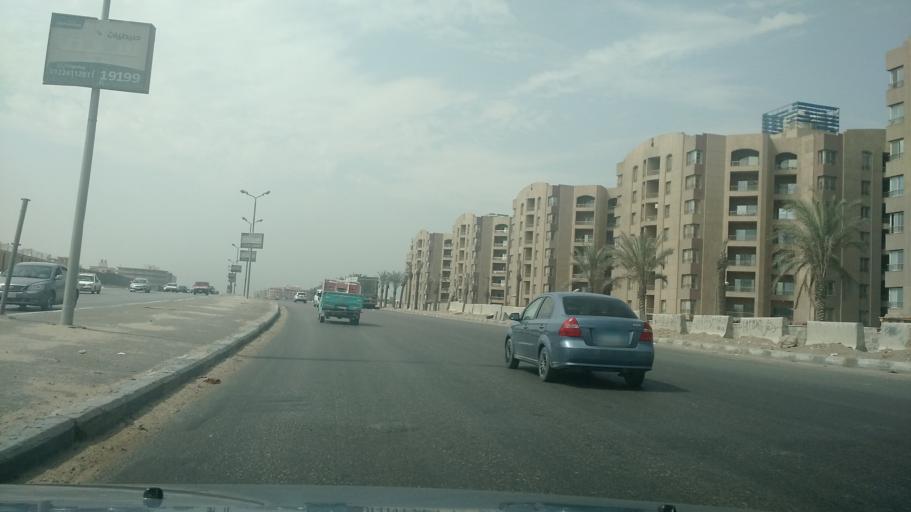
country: EG
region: Al Jizah
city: Al Hawamidiyah
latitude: 29.9671
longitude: 31.2877
